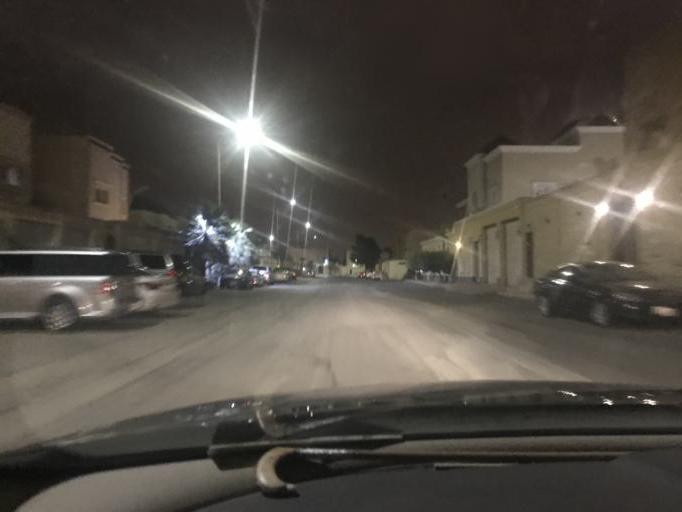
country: SA
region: Ar Riyad
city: Riyadh
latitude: 24.7987
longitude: 46.7016
